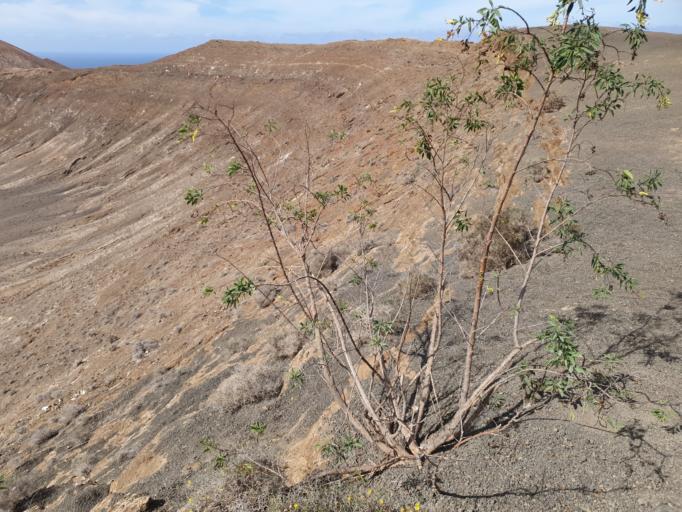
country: ES
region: Canary Islands
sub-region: Provincia de Las Palmas
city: Tinajo
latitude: 29.0429
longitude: -13.7253
